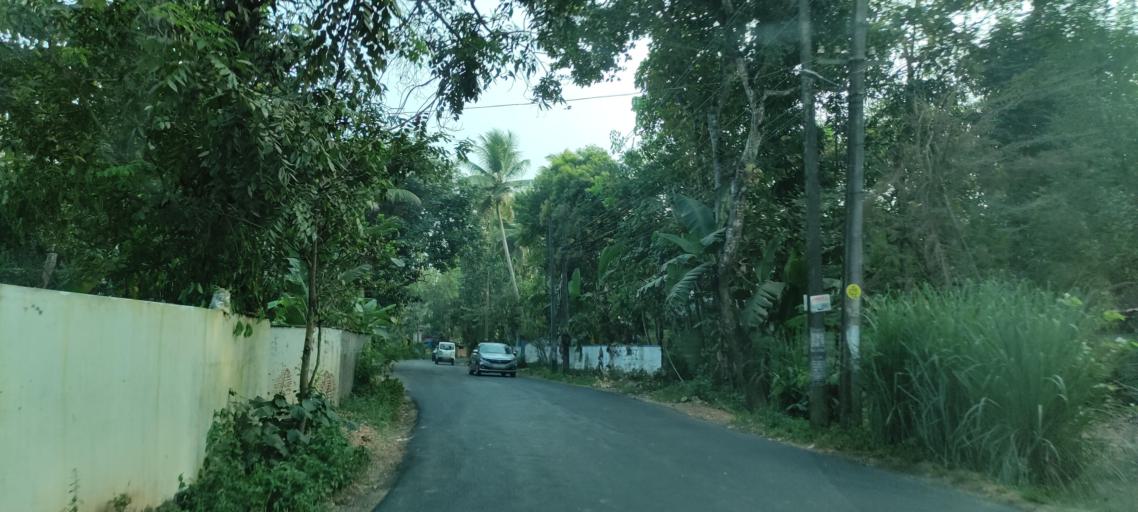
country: IN
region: Kerala
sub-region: Kottayam
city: Vaikam
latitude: 9.6891
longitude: 76.4637
